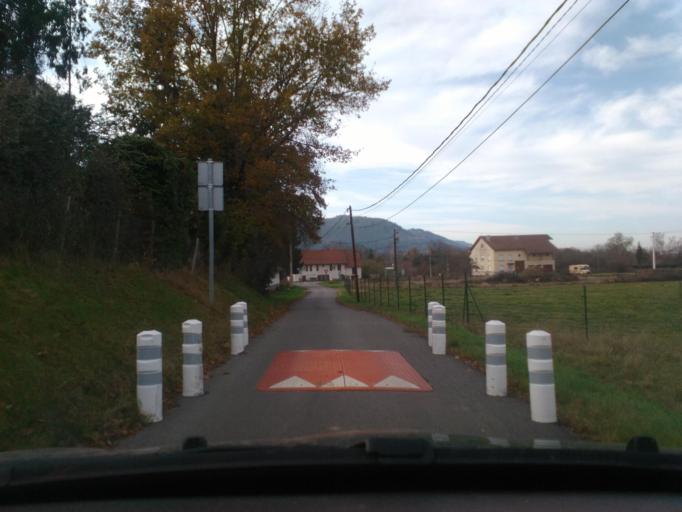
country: FR
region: Lorraine
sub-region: Departement des Vosges
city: Sainte-Marguerite
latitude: 48.2544
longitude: 6.9759
